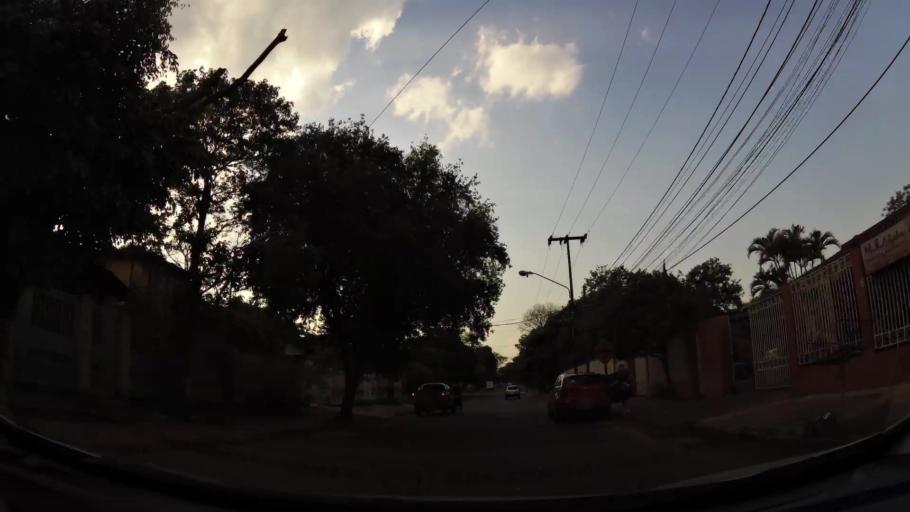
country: PY
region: Alto Parana
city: Presidente Franco
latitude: -25.5205
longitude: -54.6386
